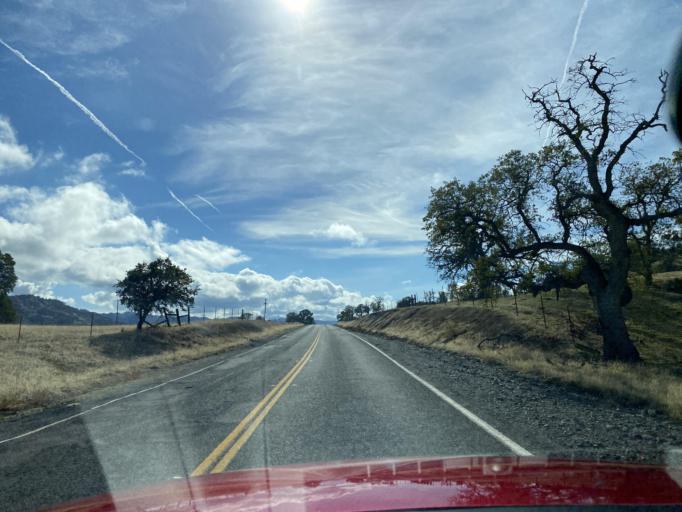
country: US
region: California
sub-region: Glenn County
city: Willows
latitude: 39.4767
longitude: -122.5144
